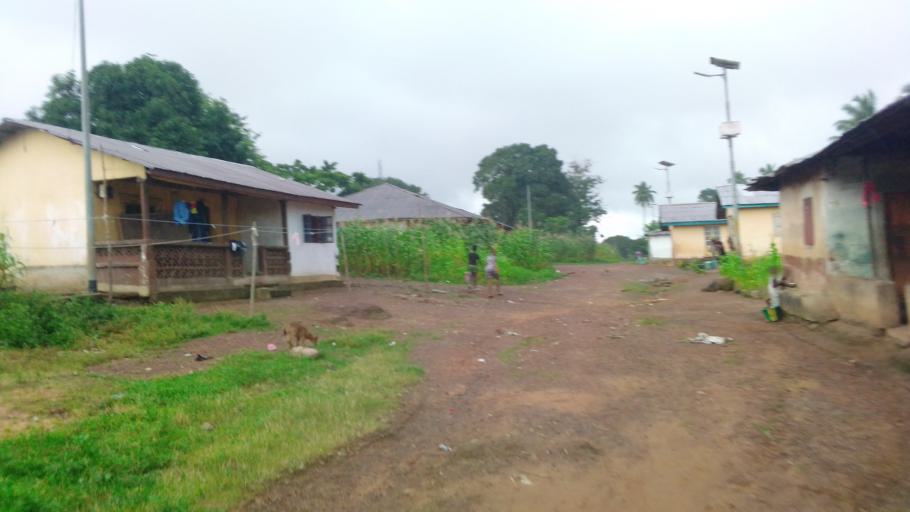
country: SL
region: Northern Province
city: Lunsar
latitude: 8.6824
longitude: -12.5322
